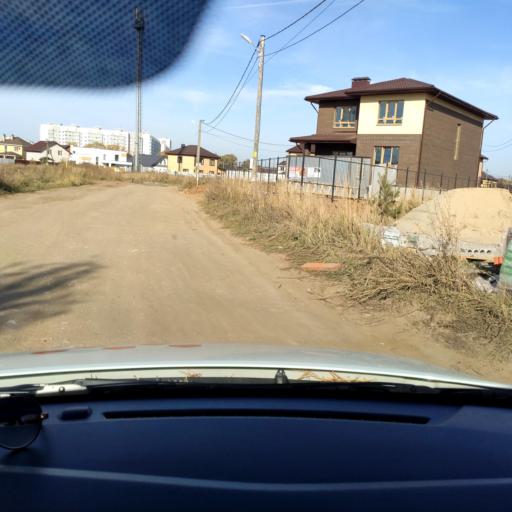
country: RU
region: Tatarstan
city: Vysokaya Gora
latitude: 55.7887
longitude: 49.2594
